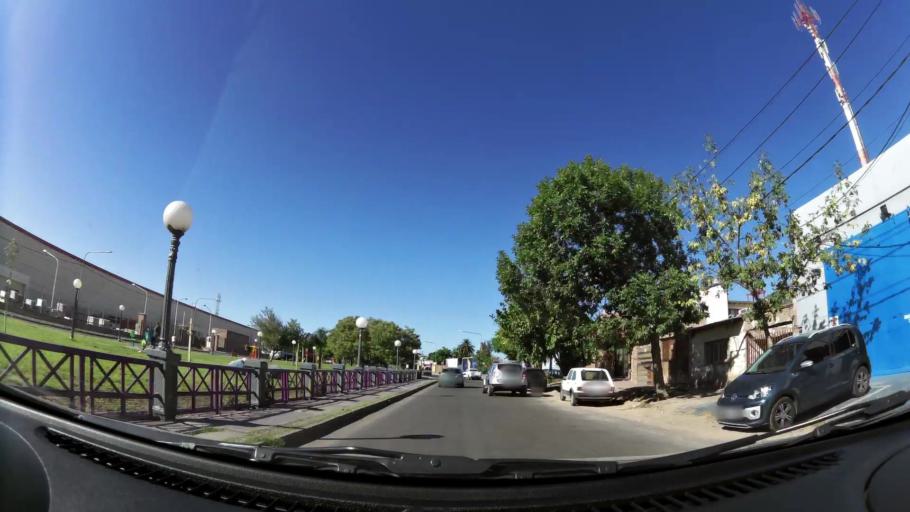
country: AR
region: Mendoza
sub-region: Departamento de Godoy Cruz
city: Godoy Cruz
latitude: -32.9166
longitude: -68.8407
